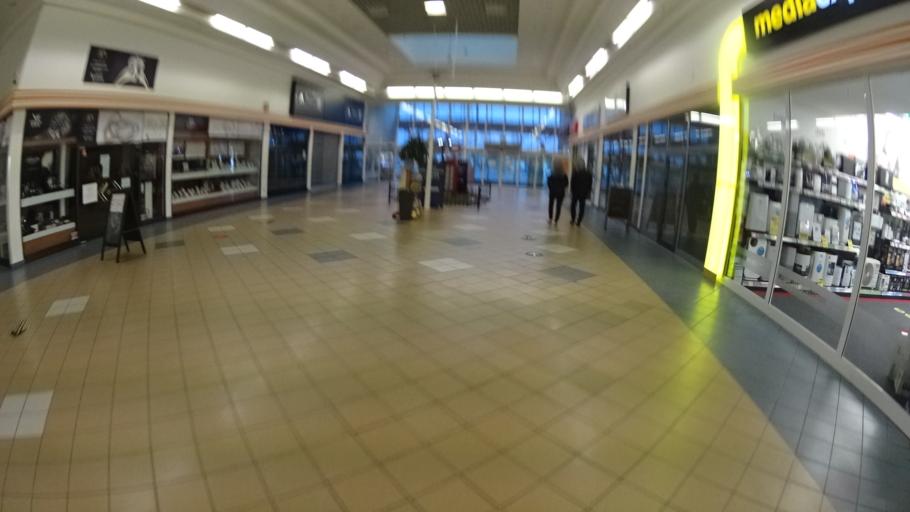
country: PL
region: Masovian Voivodeship
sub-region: Warszawa
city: Ursus
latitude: 52.2144
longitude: 20.8829
